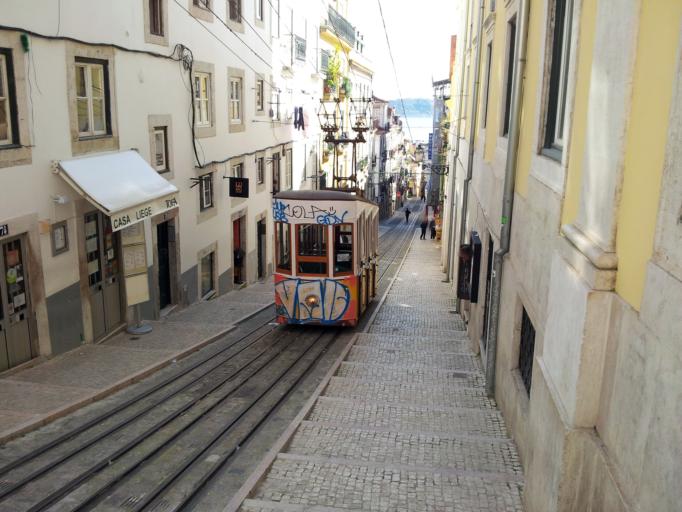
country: PT
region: Lisbon
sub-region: Lisbon
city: Lisbon
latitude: 38.7108
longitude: -9.1458
